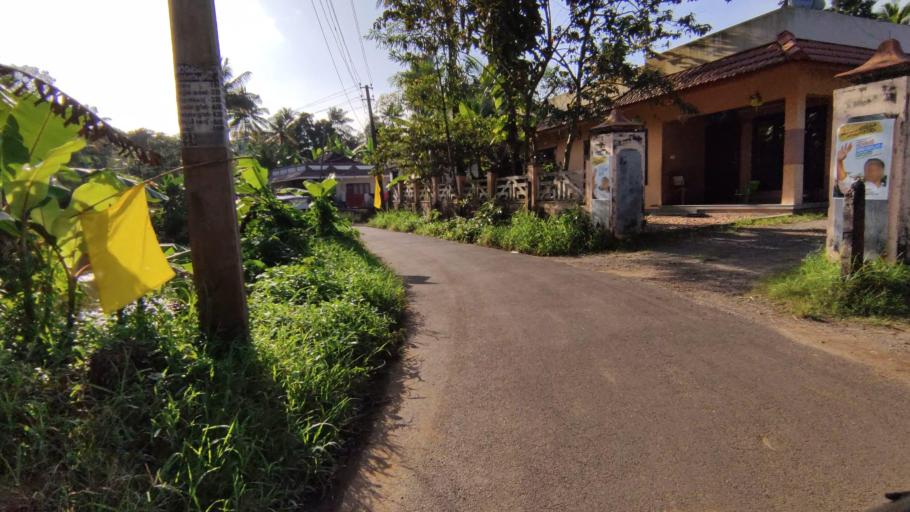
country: IN
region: Kerala
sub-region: Kottayam
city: Kottayam
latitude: 9.5977
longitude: 76.4862
